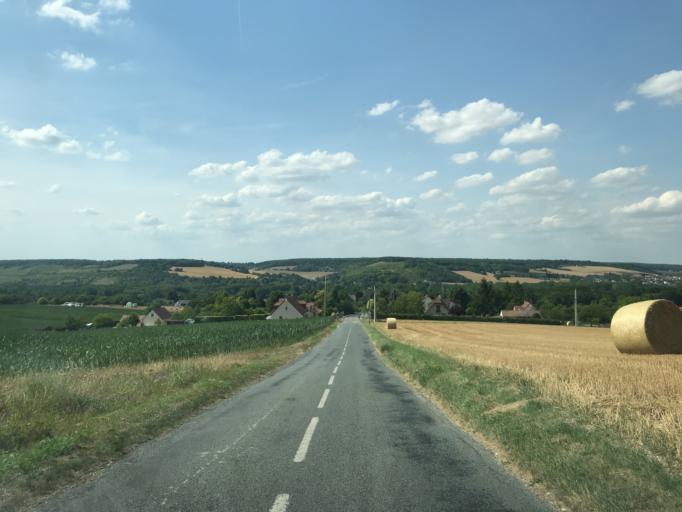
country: FR
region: Ile-de-France
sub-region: Departement des Yvelines
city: Freneuse
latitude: 49.0700
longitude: 1.5997
